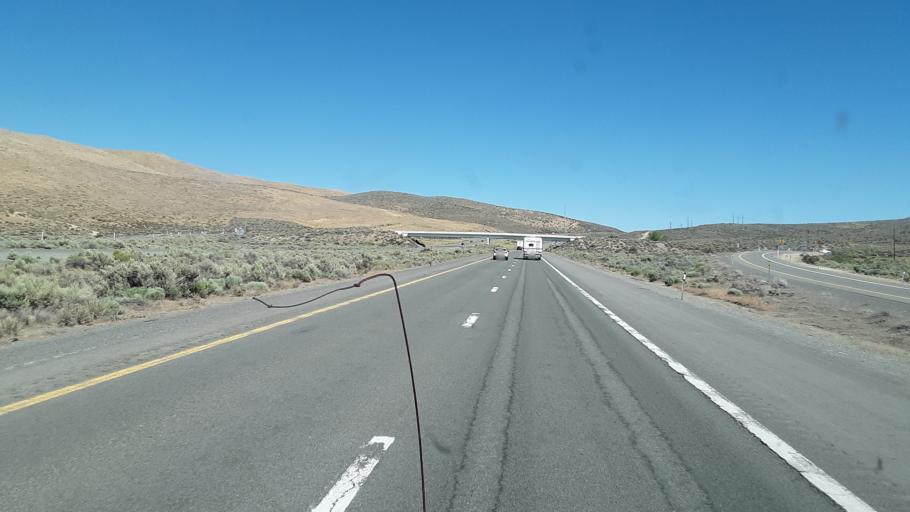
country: US
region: Nevada
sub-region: Washoe County
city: Cold Springs
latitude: 39.6450
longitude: -119.9620
